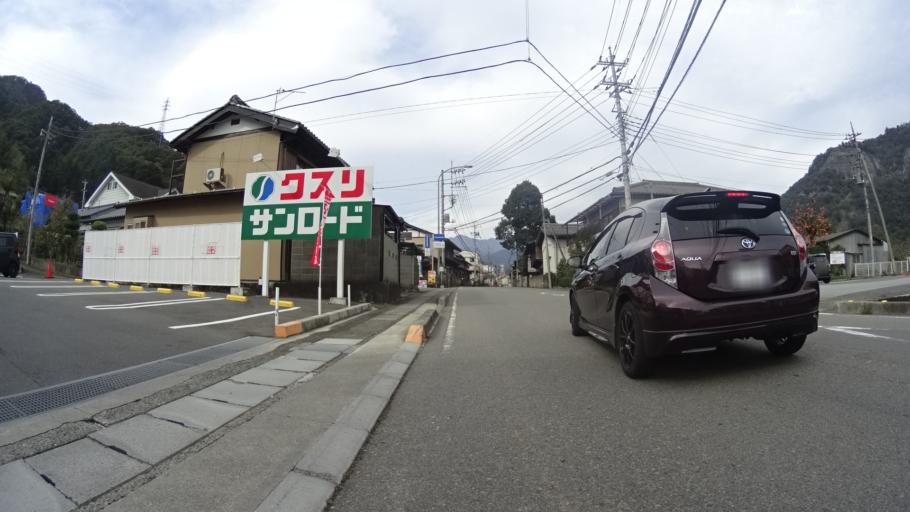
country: JP
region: Yamanashi
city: Otsuki
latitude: 35.6132
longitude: 138.9526
